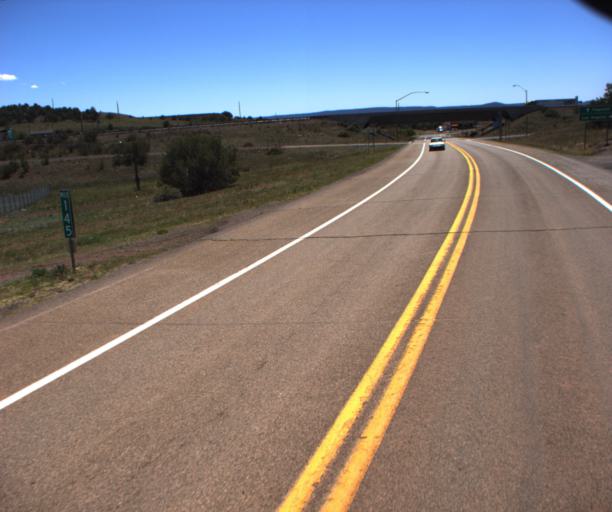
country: US
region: Arizona
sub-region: Coconino County
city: Williams
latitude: 35.2219
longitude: -112.4958
